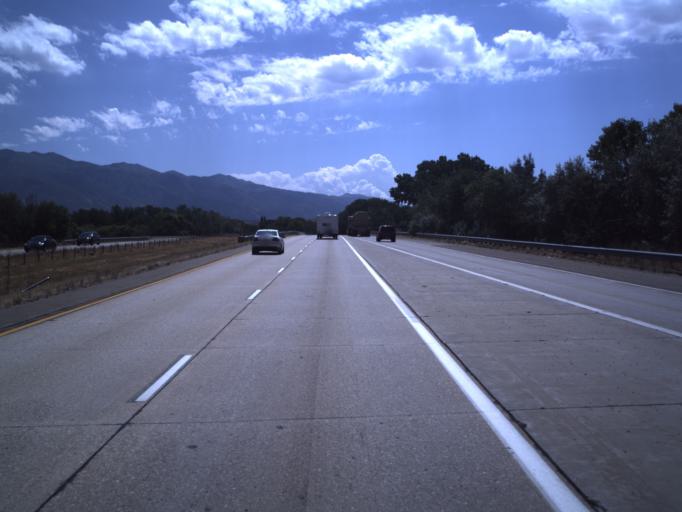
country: US
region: Utah
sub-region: Weber County
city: Riverdale
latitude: 41.1722
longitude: -112.0077
